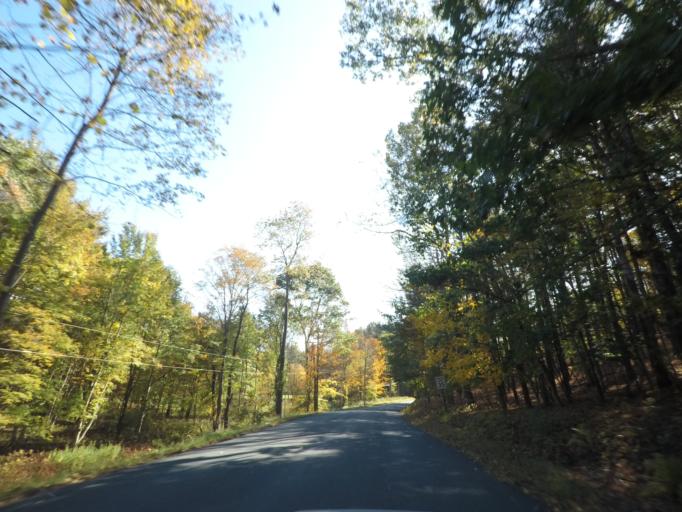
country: US
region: New York
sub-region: Rensselaer County
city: Averill Park
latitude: 42.6284
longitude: -73.5749
